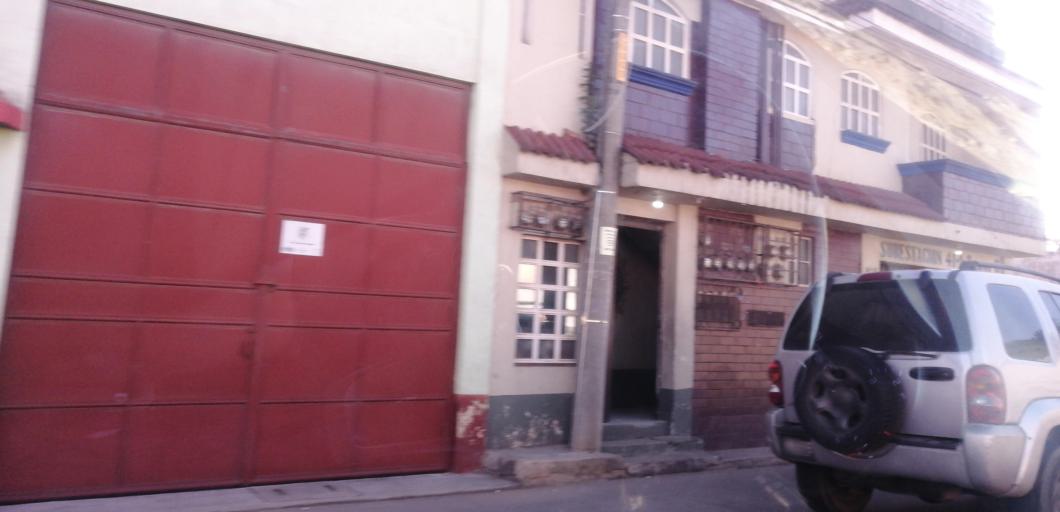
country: GT
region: Quetzaltenango
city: Olintepeque
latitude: 14.8623
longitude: -91.5371
